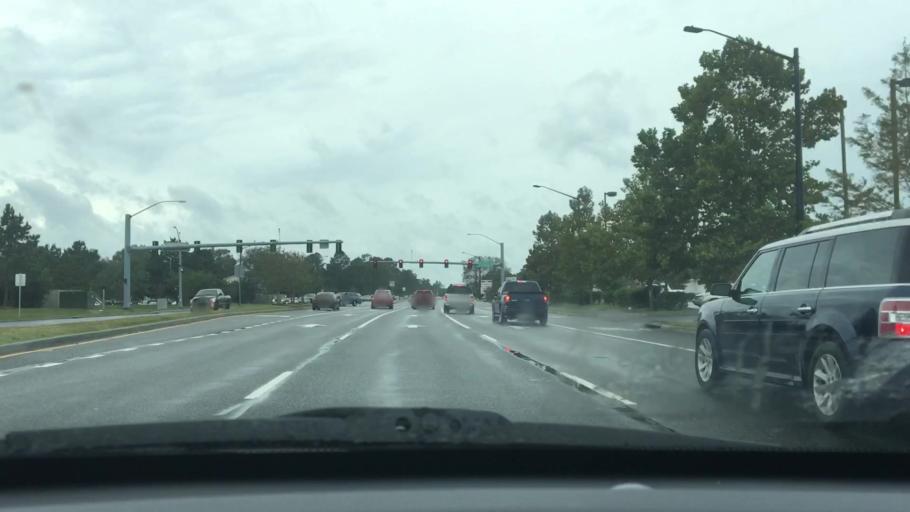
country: US
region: Virginia
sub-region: City of Virginia Beach
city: Virginia Beach
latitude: 36.8115
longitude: -76.0711
